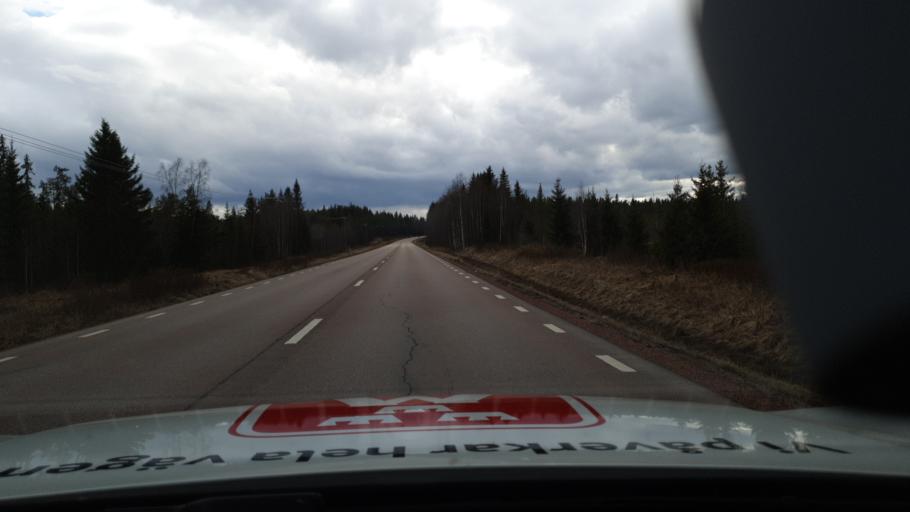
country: SE
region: Jaemtland
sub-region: Ragunda Kommun
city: Hammarstrand
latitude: 63.1757
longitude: 15.9015
